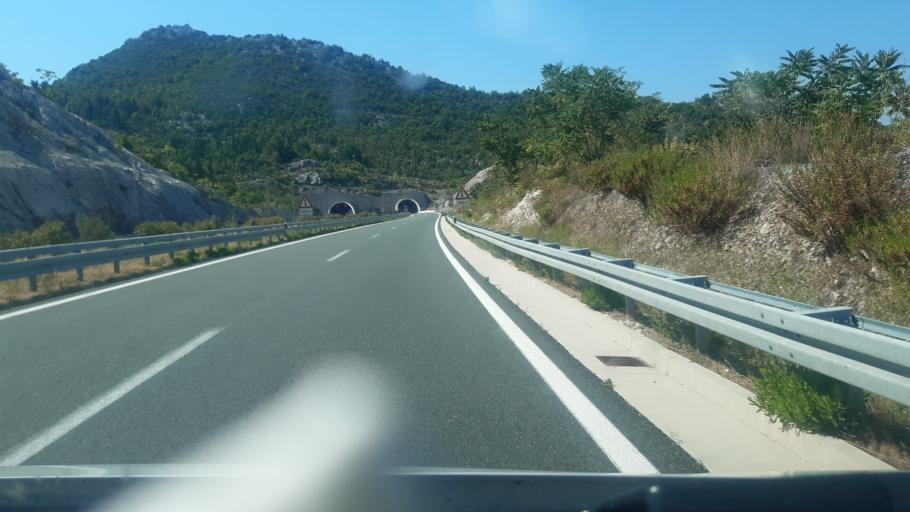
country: BA
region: Federation of Bosnia and Herzegovina
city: Ljubuski
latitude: 43.1310
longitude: 17.4845
